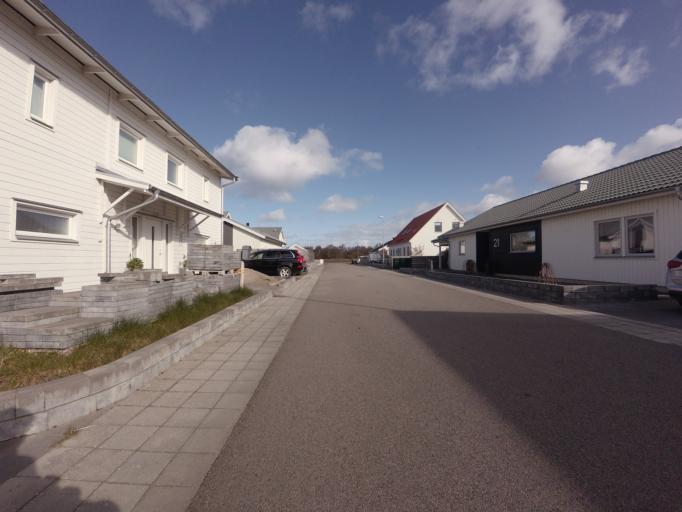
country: SE
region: Skane
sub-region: Hoganas Kommun
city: Hoganas
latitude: 56.1744
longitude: 12.5759
